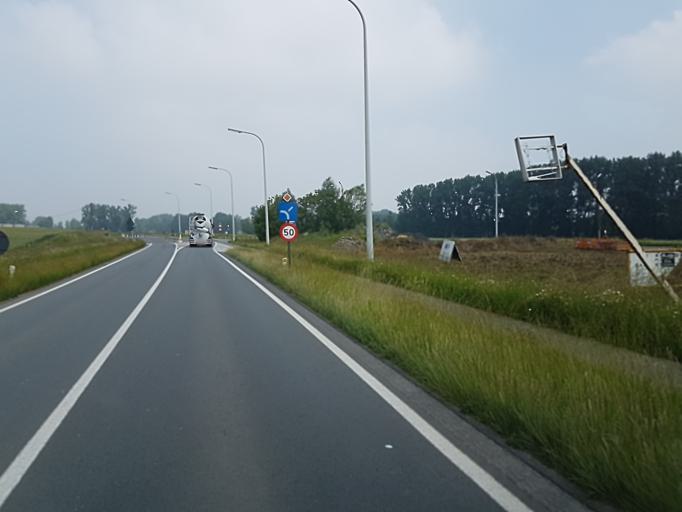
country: BE
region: Flanders
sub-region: Provincie Oost-Vlaanderen
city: Sint-Maria-Lierde
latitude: 50.8403
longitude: 3.8698
